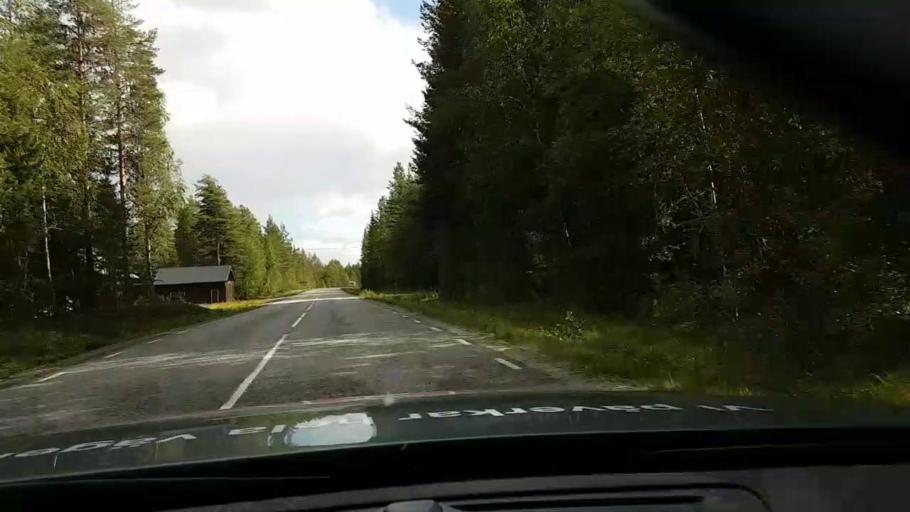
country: SE
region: Vaesternorrland
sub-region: OErnskoeldsviks Kommun
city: Bredbyn
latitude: 63.6413
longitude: 17.8981
